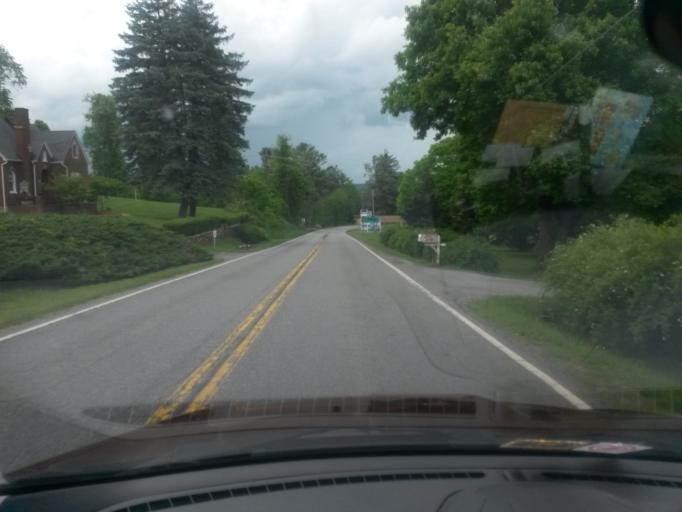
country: US
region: Virginia
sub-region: Floyd County
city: Floyd
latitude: 36.9161
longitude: -80.3223
